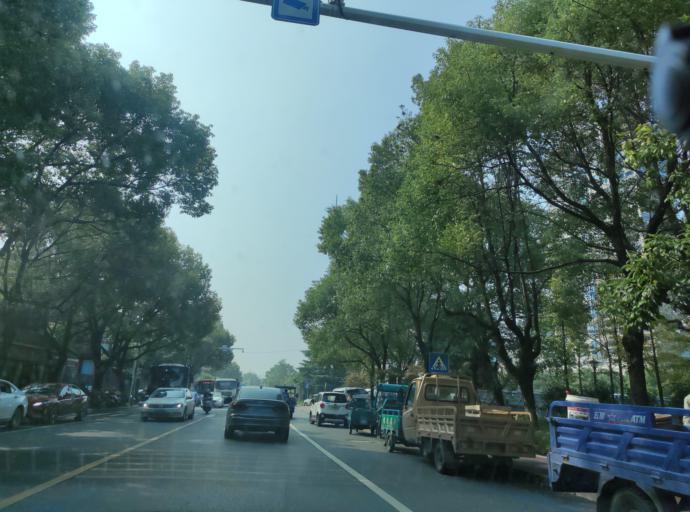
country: CN
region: Jiangxi Sheng
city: Pingxiang
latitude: 27.6407
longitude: 113.8559
